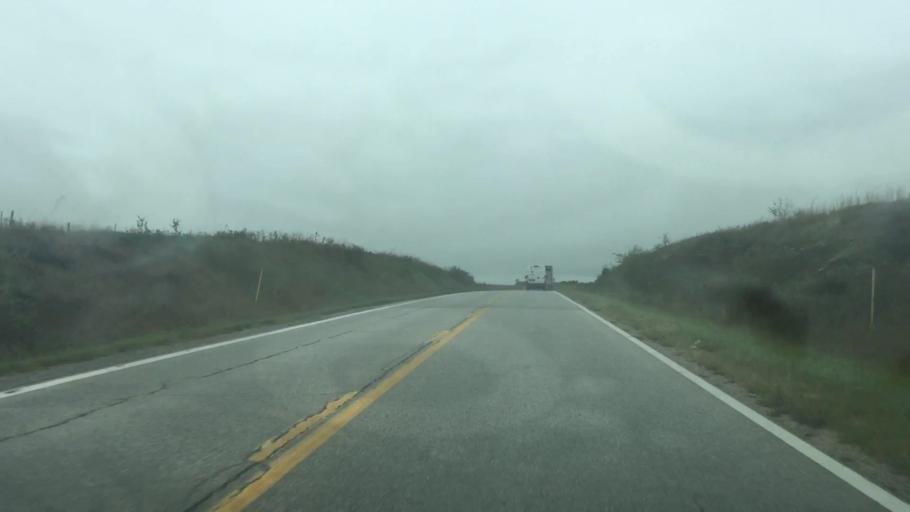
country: US
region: Kansas
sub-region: Anderson County
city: Garnett
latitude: 38.1834
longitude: -95.2610
